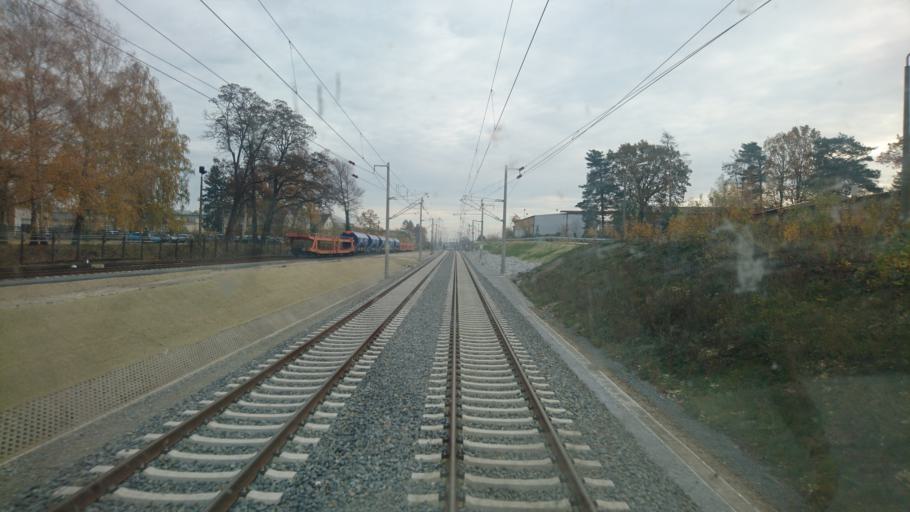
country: DE
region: Saxony
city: Niesky
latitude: 51.3003
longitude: 14.8194
